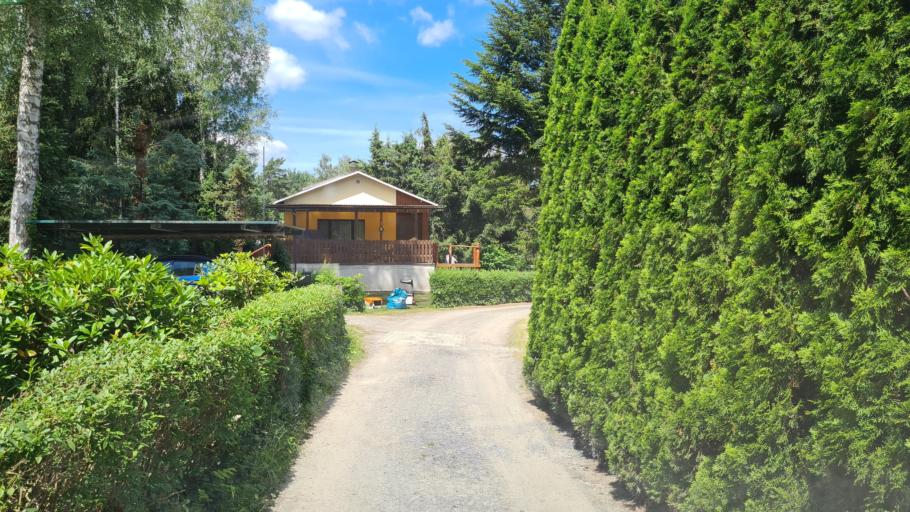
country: DE
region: Brandenburg
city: Plessa
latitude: 51.5169
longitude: 13.6534
